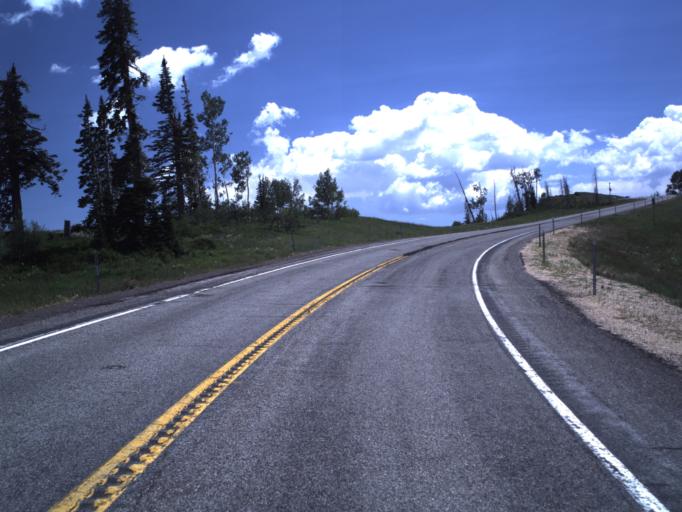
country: US
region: Utah
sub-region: Sanpete County
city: Fairview
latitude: 39.6239
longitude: -111.3165
